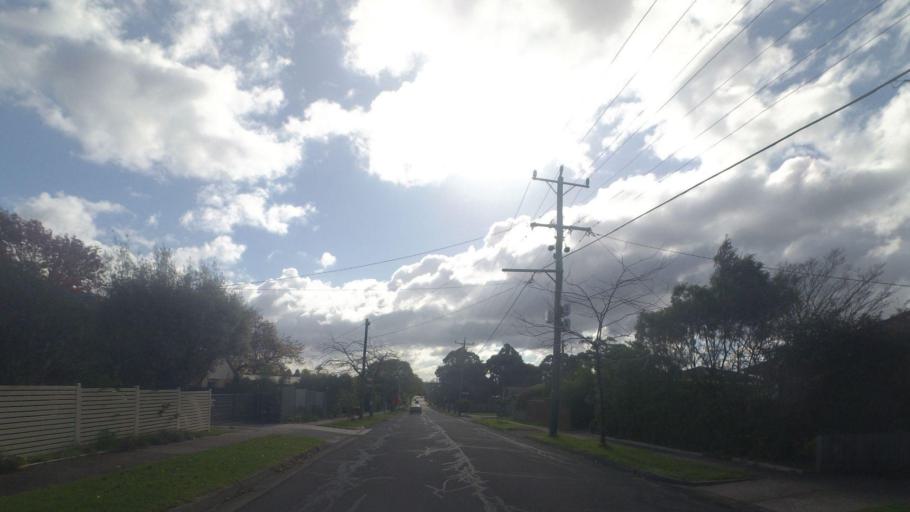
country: AU
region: Victoria
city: Forest Hill
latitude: -37.8418
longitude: 145.1831
